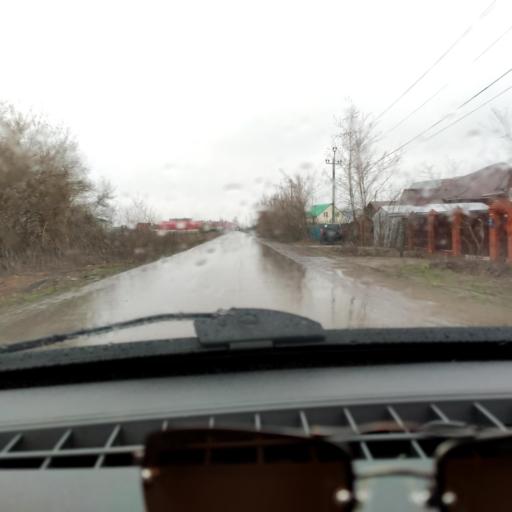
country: RU
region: Bashkortostan
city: Kabakovo
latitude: 54.5553
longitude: 56.0433
